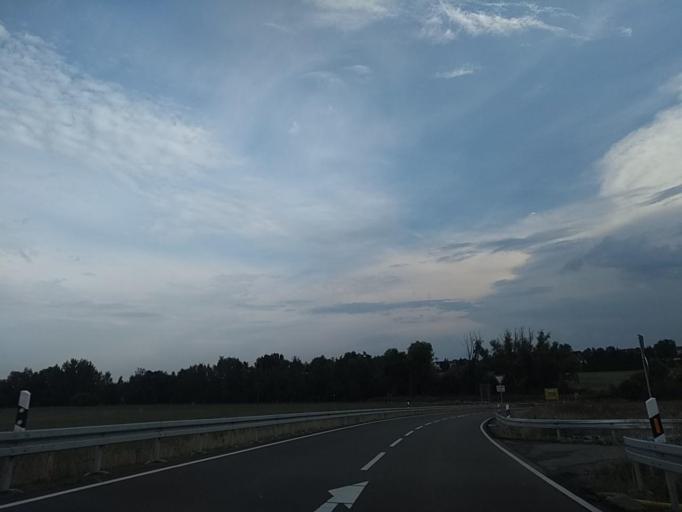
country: DE
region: Saxony-Anhalt
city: Hohenmolsen
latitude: 51.1616
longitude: 12.1130
